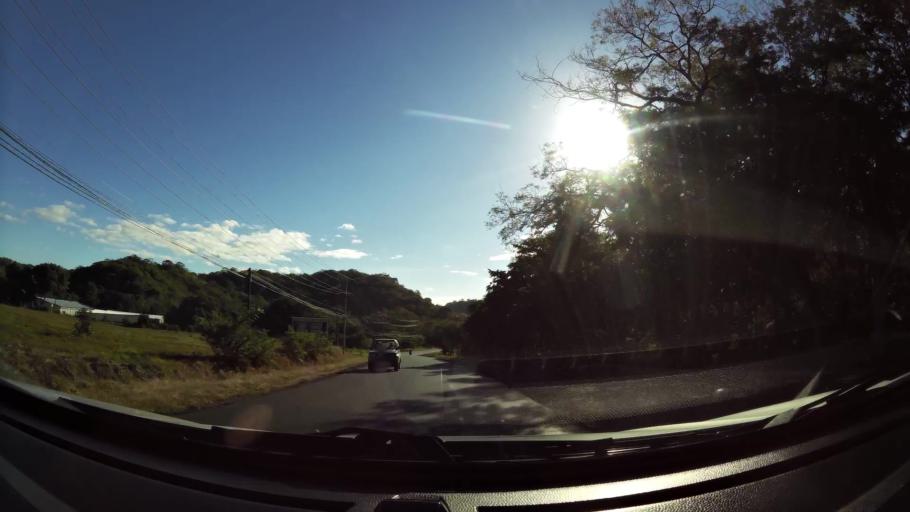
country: CR
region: Guanacaste
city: Sardinal
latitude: 10.5371
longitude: -85.6675
